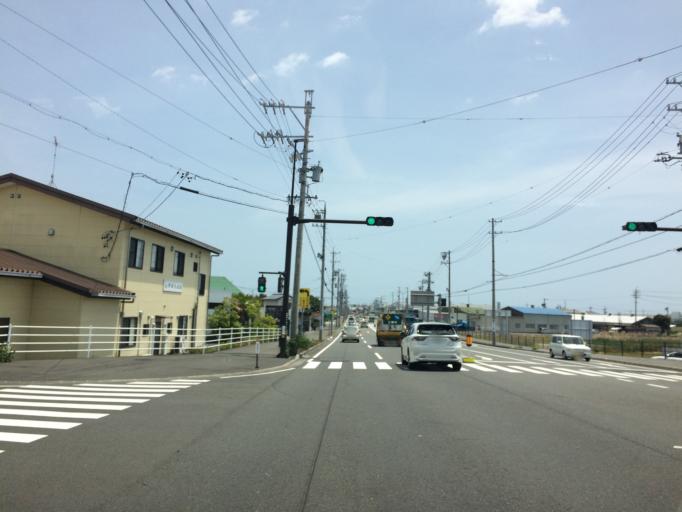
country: JP
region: Shizuoka
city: Fujieda
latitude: 34.8924
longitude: 138.2843
